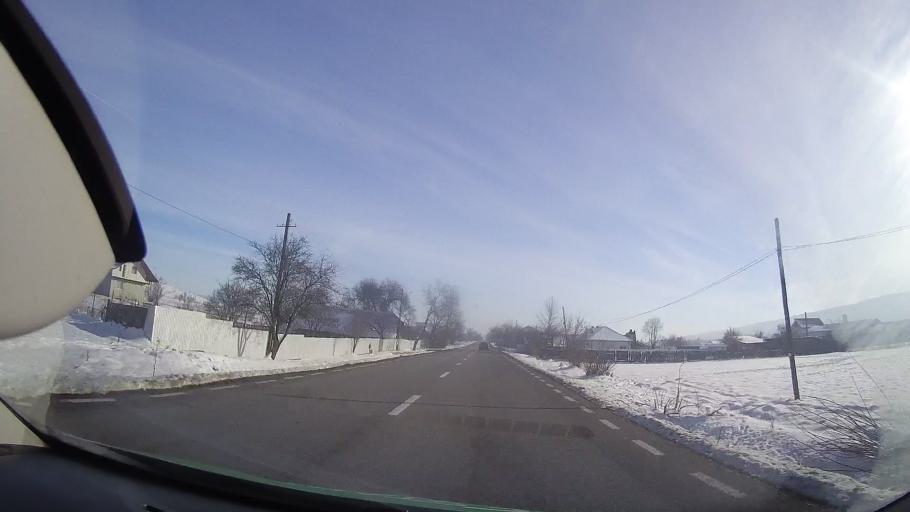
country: RO
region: Neamt
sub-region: Comuna Negresti
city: Negresti
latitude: 47.0626
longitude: 26.3807
